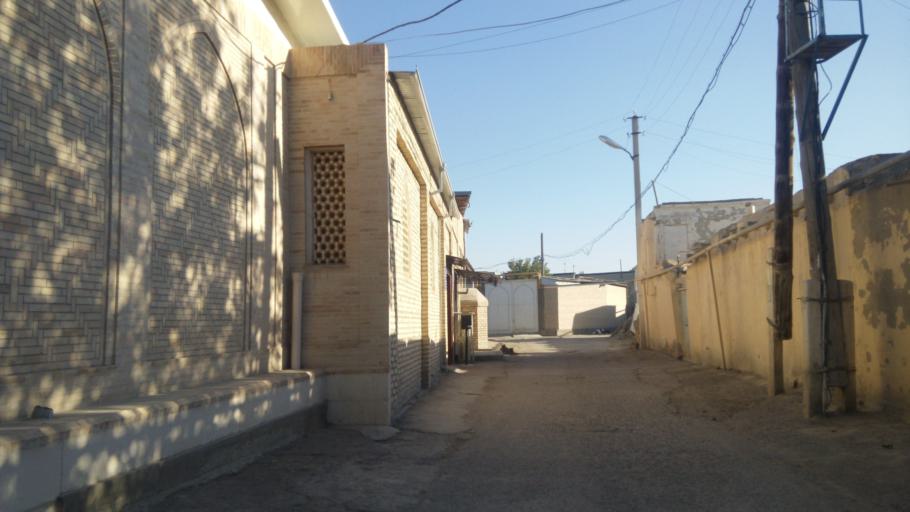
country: UZ
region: Bukhara
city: Bukhara
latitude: 39.7757
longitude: 64.4255
